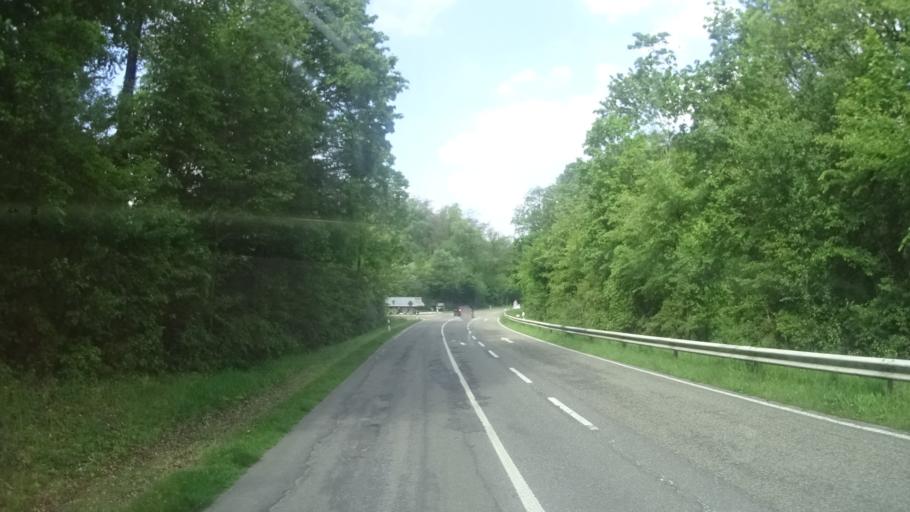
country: DE
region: Baden-Wuerttemberg
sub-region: Karlsruhe Region
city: Balzfeld
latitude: 49.1931
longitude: 8.8191
